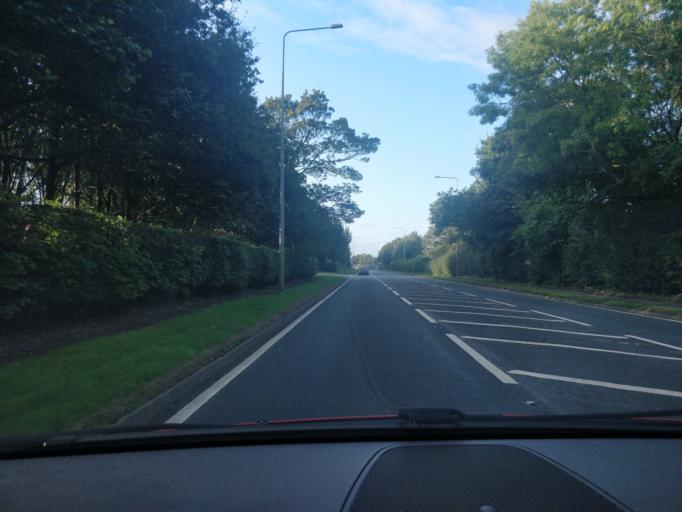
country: GB
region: England
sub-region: Lancashire
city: Tarleton
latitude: 53.6816
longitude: -2.8168
